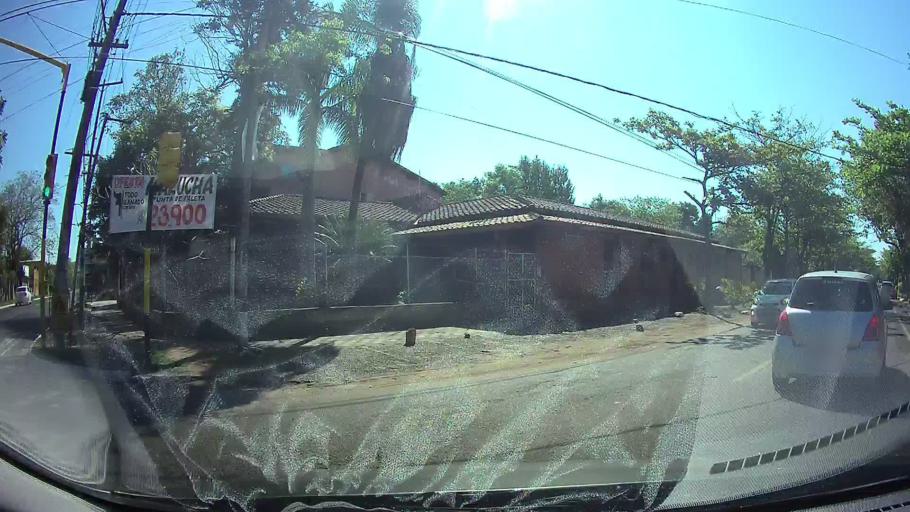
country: PY
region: Central
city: Ypacarai
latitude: -25.4016
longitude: -57.2904
